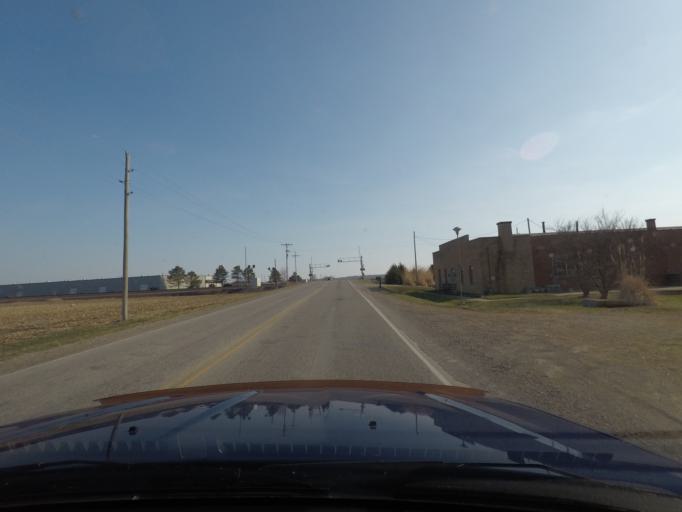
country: US
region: Kansas
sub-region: Jefferson County
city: Oskaloosa
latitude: 39.0722
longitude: -95.3820
